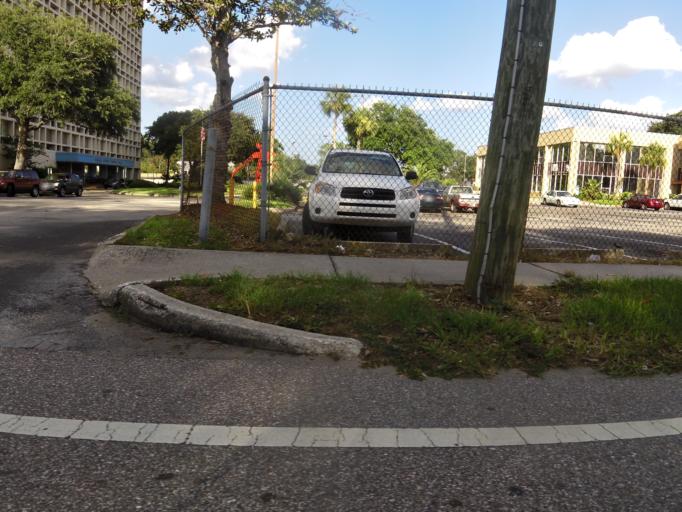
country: US
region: Florida
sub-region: Duval County
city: Jacksonville
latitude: 30.3407
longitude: -81.6630
